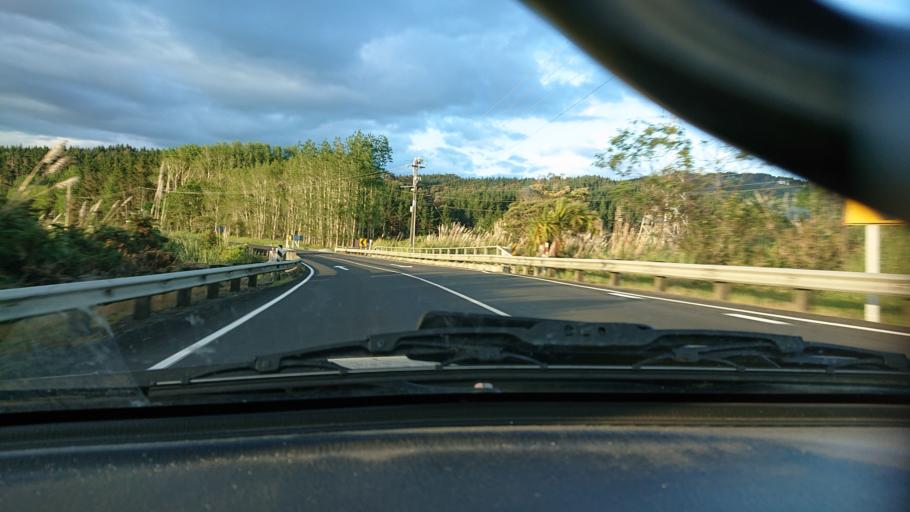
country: NZ
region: Auckland
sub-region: Auckland
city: Parakai
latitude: -36.5077
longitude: 174.4569
